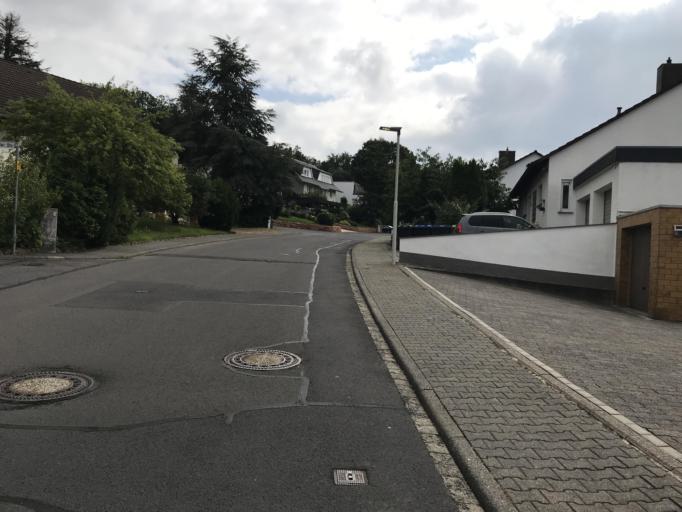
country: DE
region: Hesse
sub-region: Regierungsbezirk Giessen
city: Lauterbach
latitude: 50.6228
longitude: 9.3968
